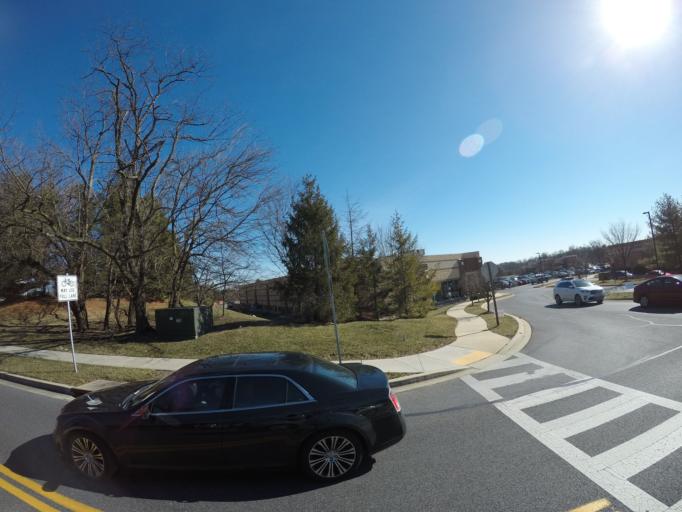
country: US
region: Maryland
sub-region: Howard County
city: Columbia
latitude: 39.2011
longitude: -76.8134
